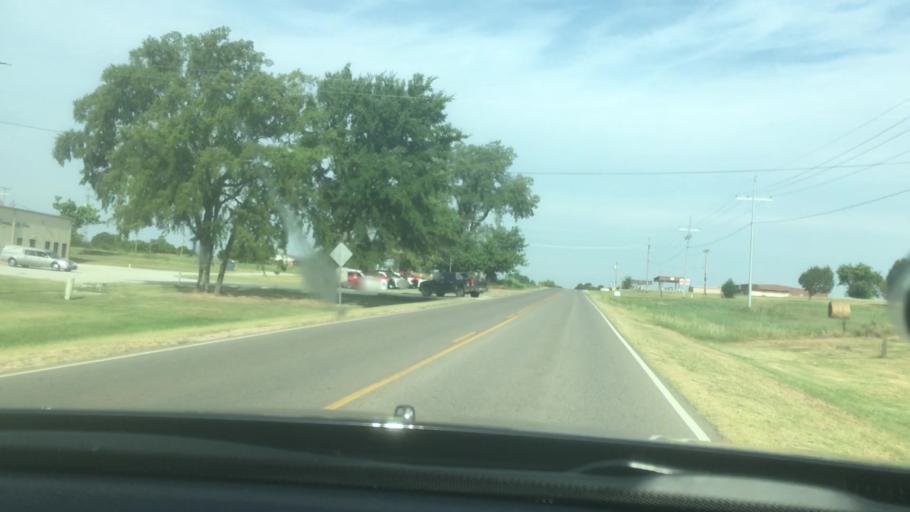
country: US
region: Oklahoma
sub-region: Pontotoc County
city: Ada
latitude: 34.7821
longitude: -96.7778
